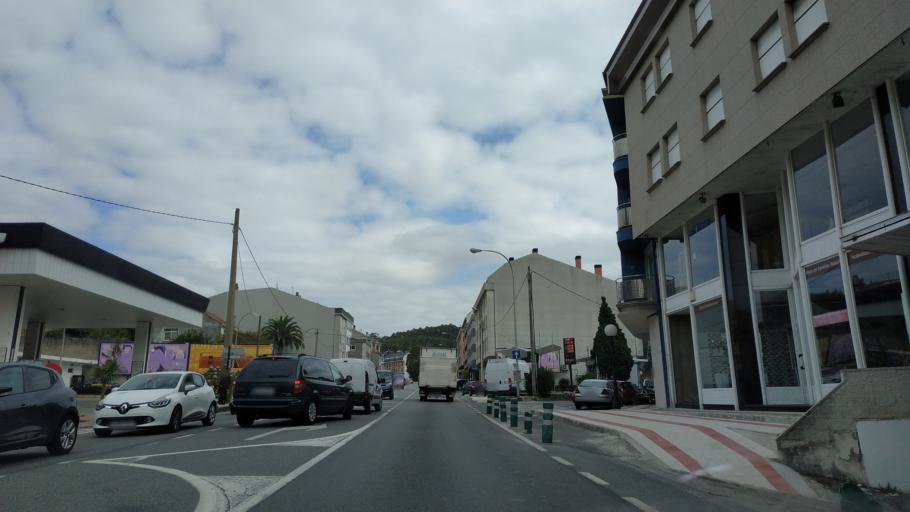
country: ES
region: Galicia
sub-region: Provincia da Coruna
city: Arteixo
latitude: 43.3172
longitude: -8.4796
